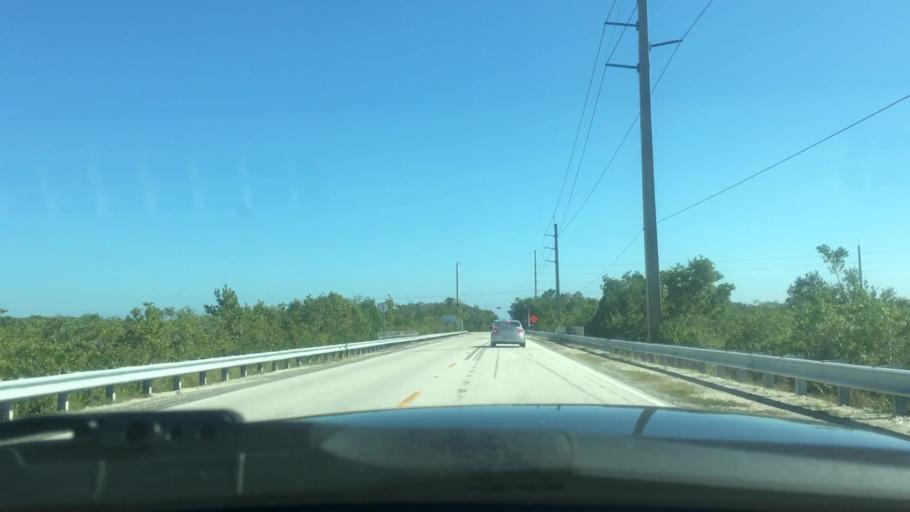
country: US
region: Florida
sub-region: Monroe County
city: North Key Largo
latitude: 25.2855
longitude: -80.3063
